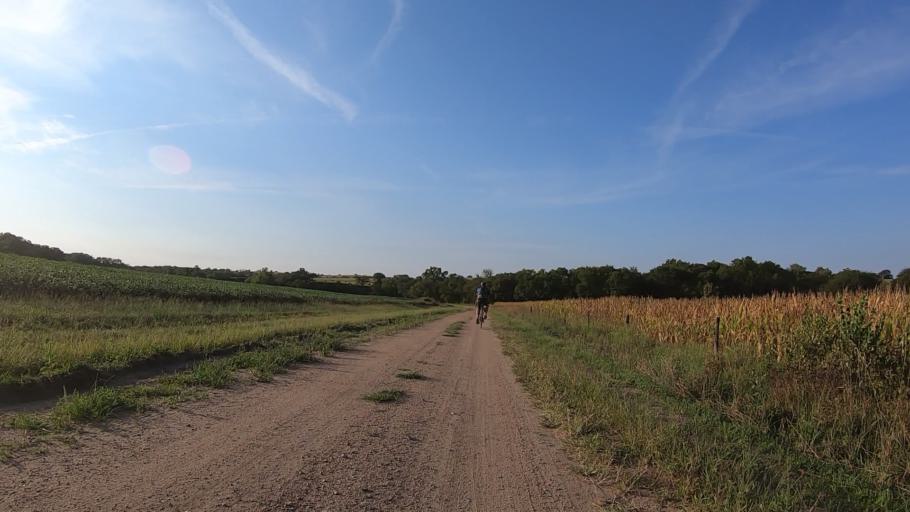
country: US
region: Kansas
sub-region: Marshall County
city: Blue Rapids
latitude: 39.7238
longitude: -96.8070
